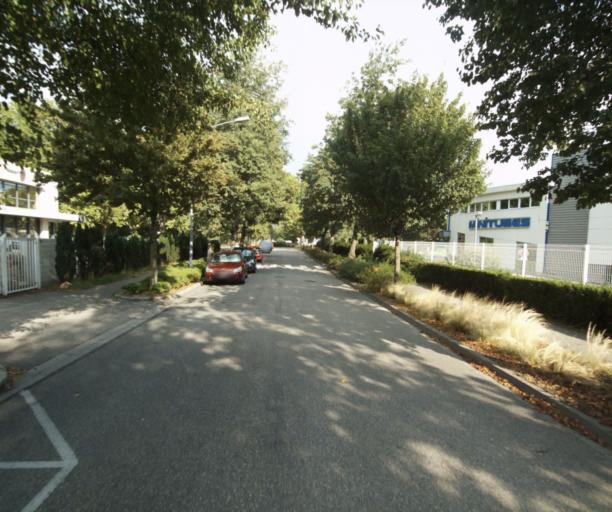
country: FR
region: Rhone-Alpes
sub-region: Departement de l'Isere
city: Grenoble
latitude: 45.1612
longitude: 5.7062
